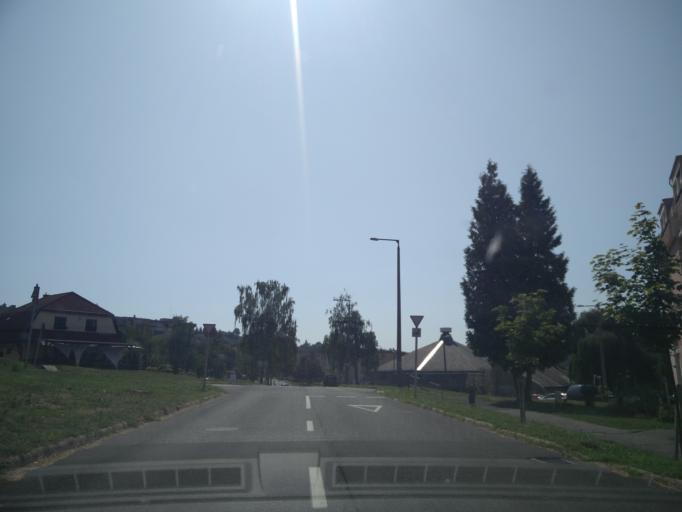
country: HU
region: Zala
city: Zalaegerszeg
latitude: 46.8262
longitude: 16.8296
